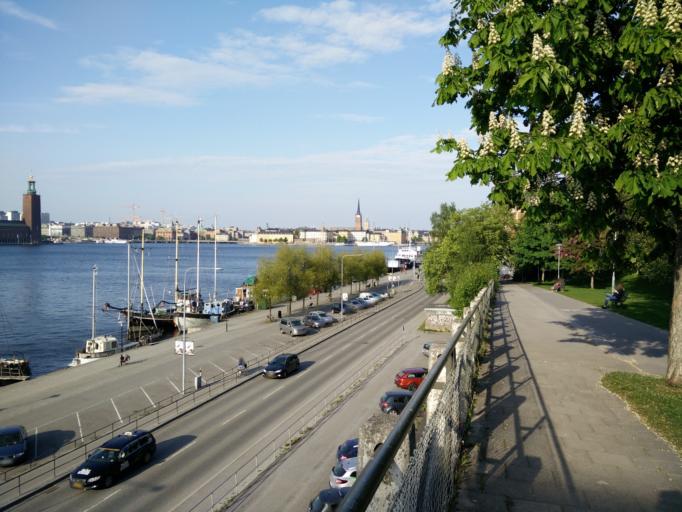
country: SE
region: Stockholm
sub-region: Stockholms Kommun
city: Stockholm
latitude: 59.3206
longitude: 18.0470
